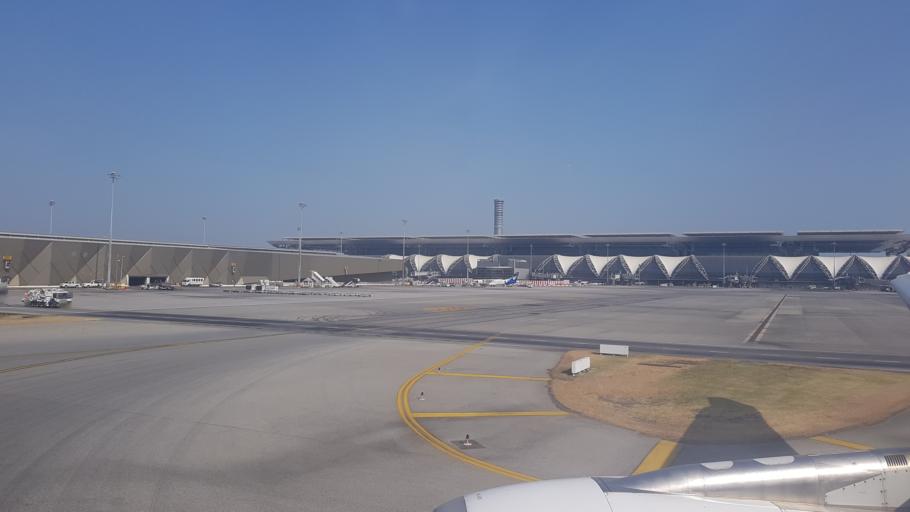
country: TH
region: Bangkok
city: Lat Krabang
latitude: 13.6860
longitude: 100.7510
